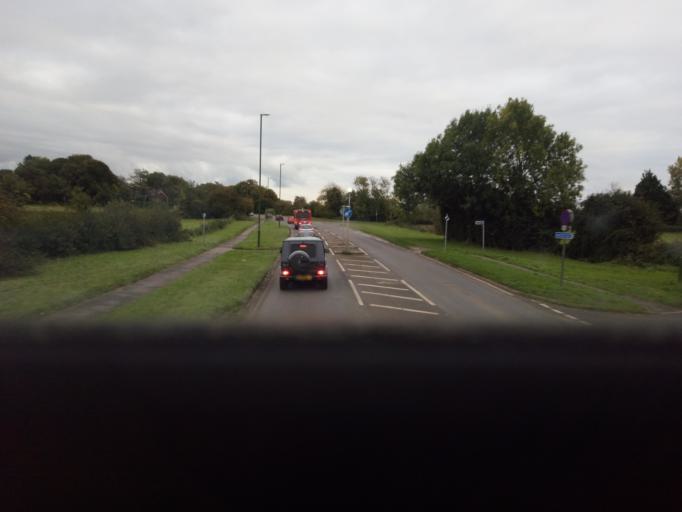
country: GB
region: England
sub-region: West Sussex
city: Boxgrove
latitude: 50.8238
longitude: -0.7319
